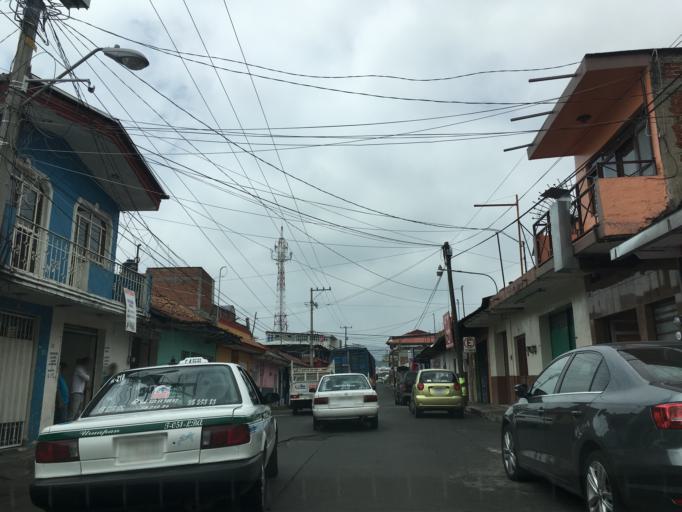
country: MX
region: Michoacan
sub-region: Uruapan
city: Uruapan
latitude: 19.4204
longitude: -102.0544
